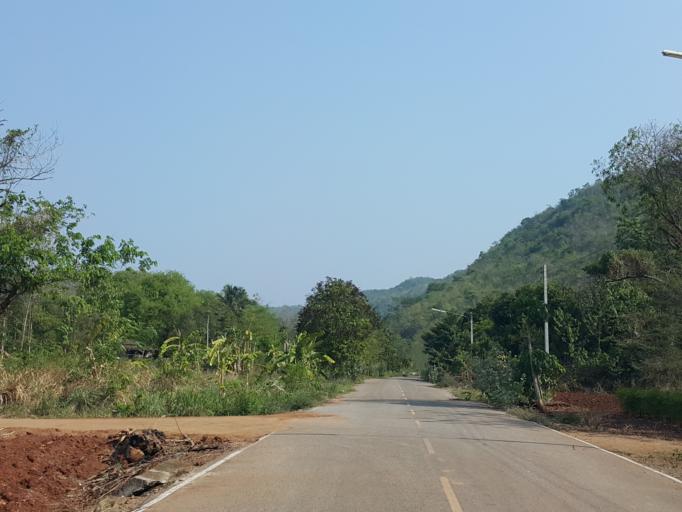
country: TH
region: Kanchanaburi
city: Sai Yok
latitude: 14.1297
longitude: 99.1297
